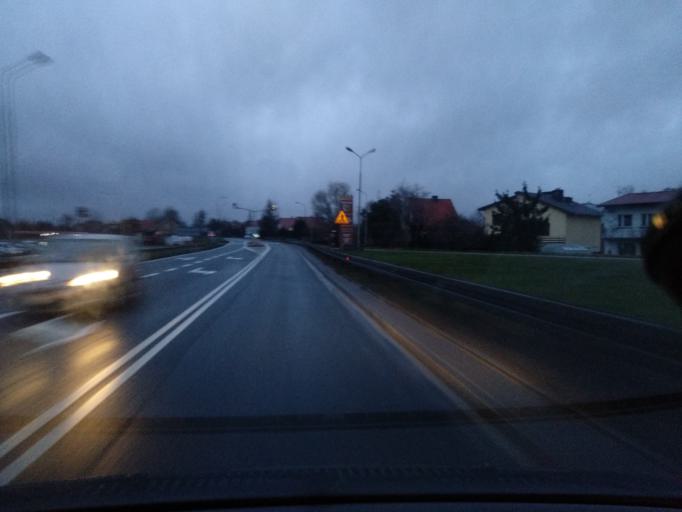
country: PL
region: Lower Silesian Voivodeship
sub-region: Powiat sredzki
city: Sroda Slaska
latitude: 51.1626
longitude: 16.5799
